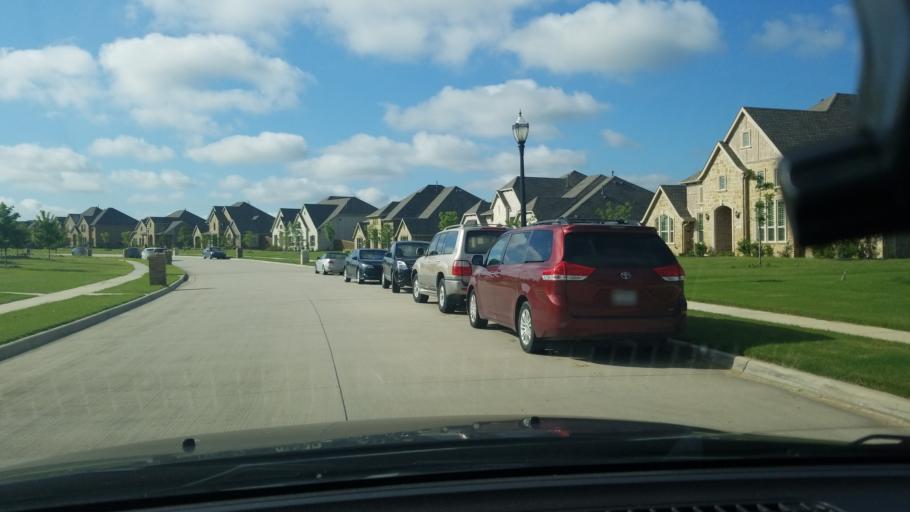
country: US
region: Texas
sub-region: Dallas County
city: Sunnyvale
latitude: 32.8031
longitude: -96.5654
